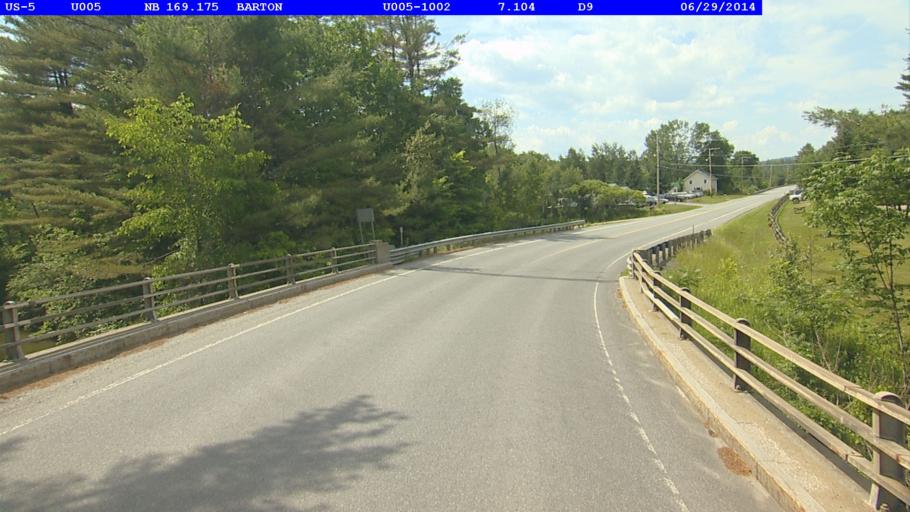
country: US
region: Vermont
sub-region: Orleans County
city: Newport
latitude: 44.7618
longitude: -72.2023
